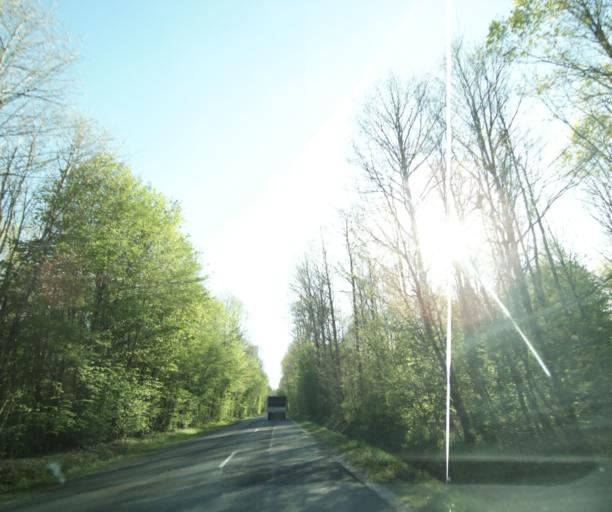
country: FR
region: Ile-de-France
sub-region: Departement de Seine-et-Marne
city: La Chapelle-Gauthier
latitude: 48.4990
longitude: 2.9077
